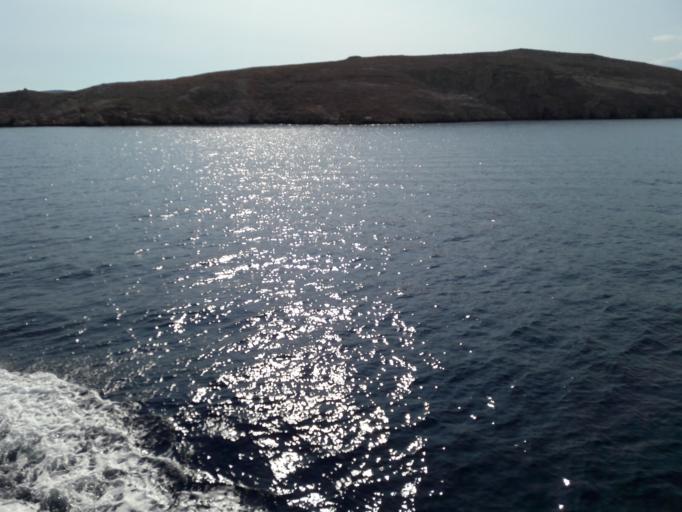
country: HR
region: Primorsko-Goranska
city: Banjol
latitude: 44.7060
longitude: 14.8723
